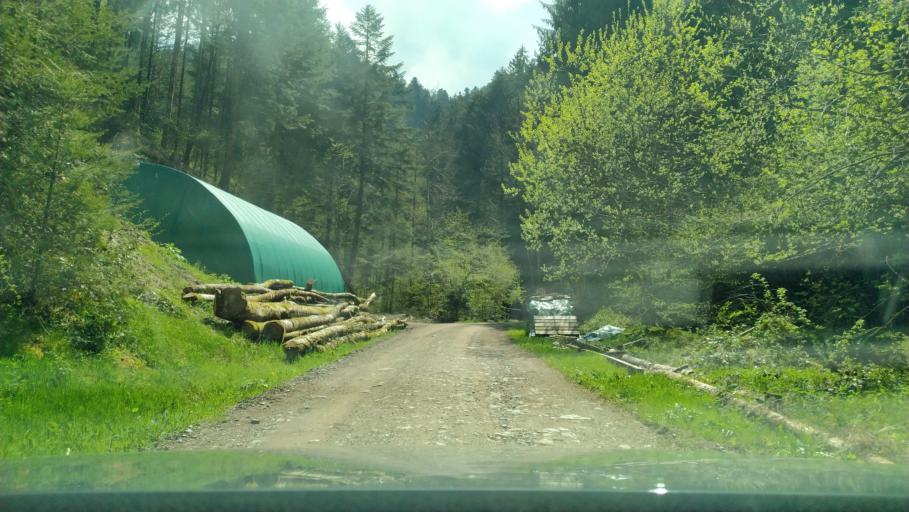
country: DE
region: Baden-Wuerttemberg
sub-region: Freiburg Region
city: Gutenbach
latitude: 48.0639
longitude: 8.1061
